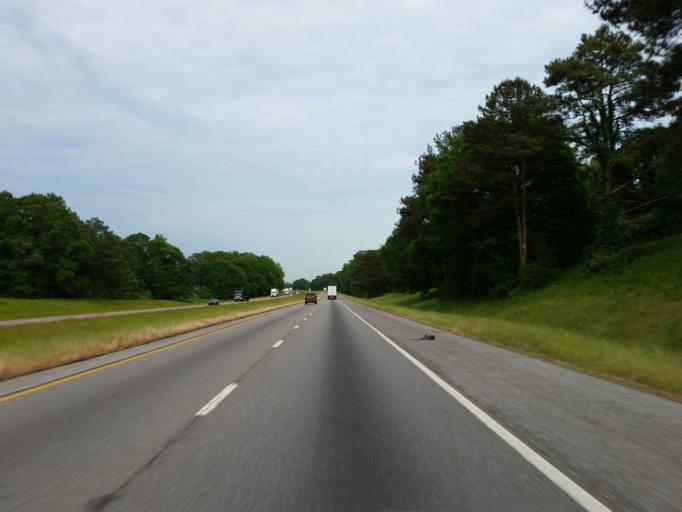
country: US
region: Alabama
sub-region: Talladega County
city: Lincoln
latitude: 33.5870
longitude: -86.0869
